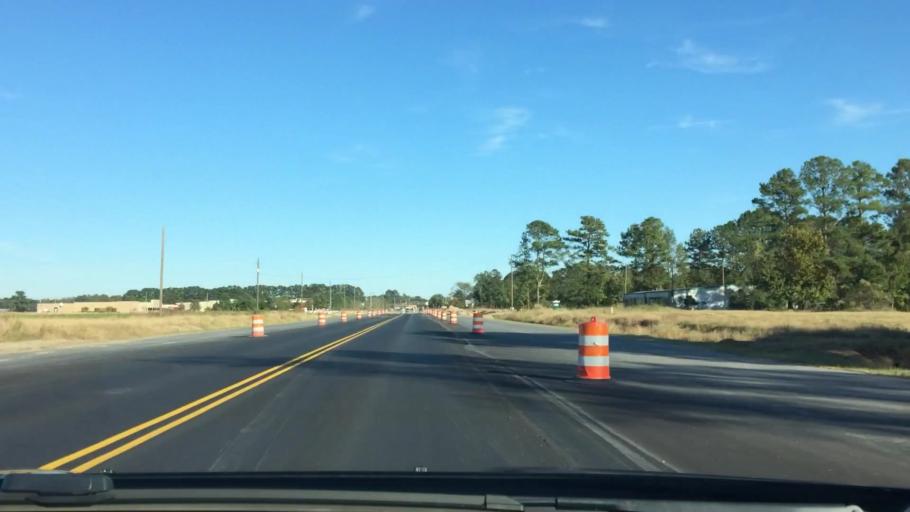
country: US
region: North Carolina
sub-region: Pitt County
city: Ayden
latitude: 35.4762
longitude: -77.4428
